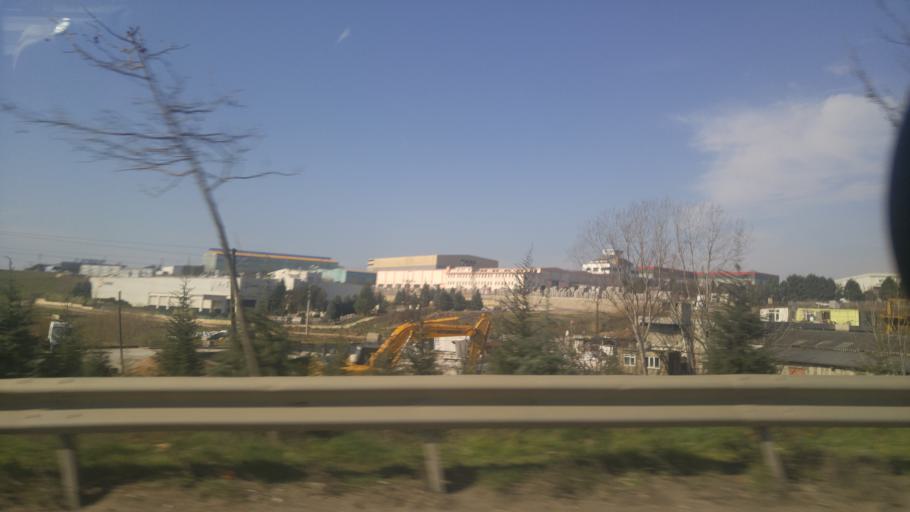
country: TR
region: Kocaeli
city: Balcik
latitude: 40.8507
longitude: 29.3746
